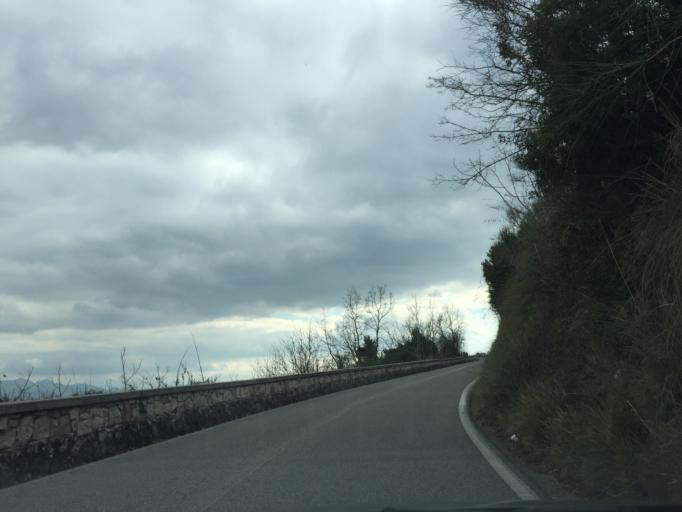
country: IT
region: Latium
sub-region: Provincia di Frosinone
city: Cassino
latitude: 41.4926
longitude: 13.8202
